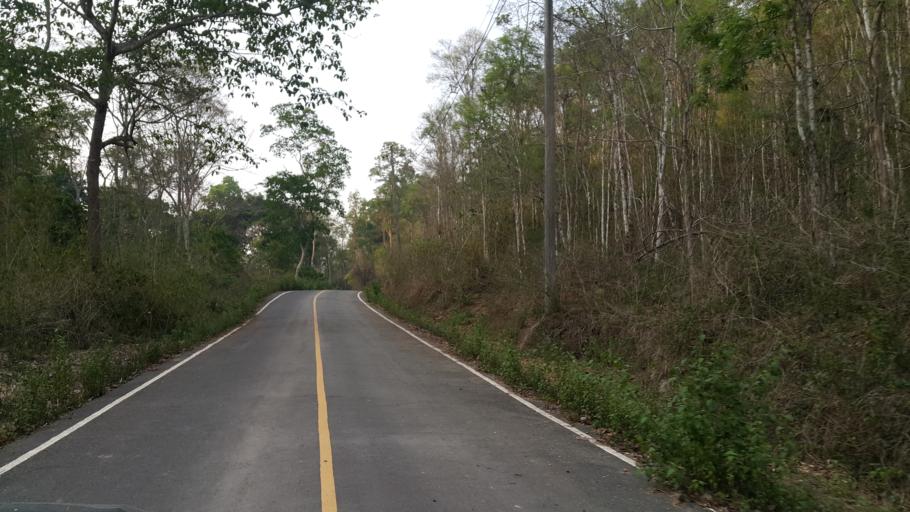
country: TH
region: Chiang Mai
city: Mae On
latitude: 18.7863
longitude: 99.2964
